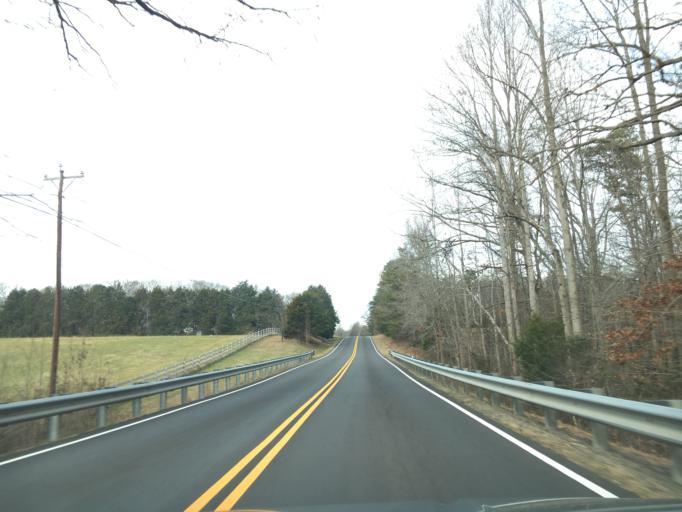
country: US
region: Virginia
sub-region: Goochland County
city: Goochland
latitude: 37.7380
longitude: -77.8430
